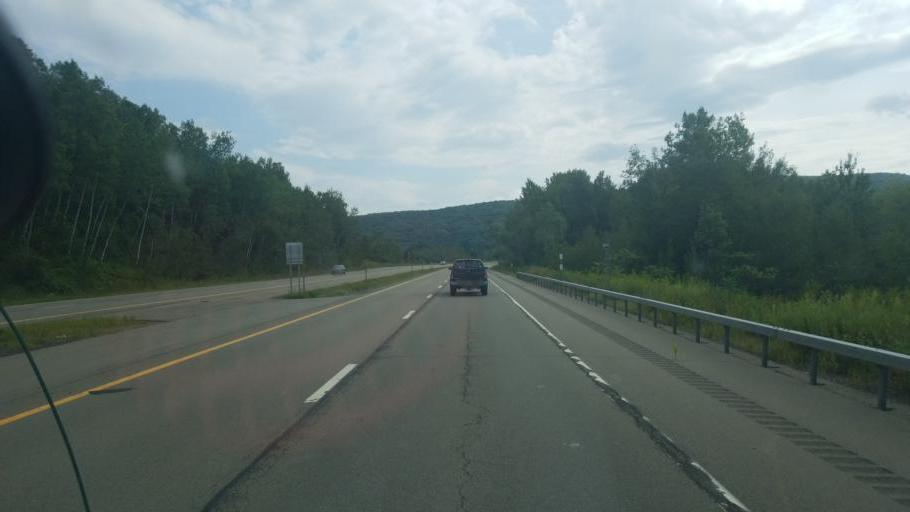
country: US
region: New York
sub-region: Cattaraugus County
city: Salamanca
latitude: 42.1164
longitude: -78.7778
